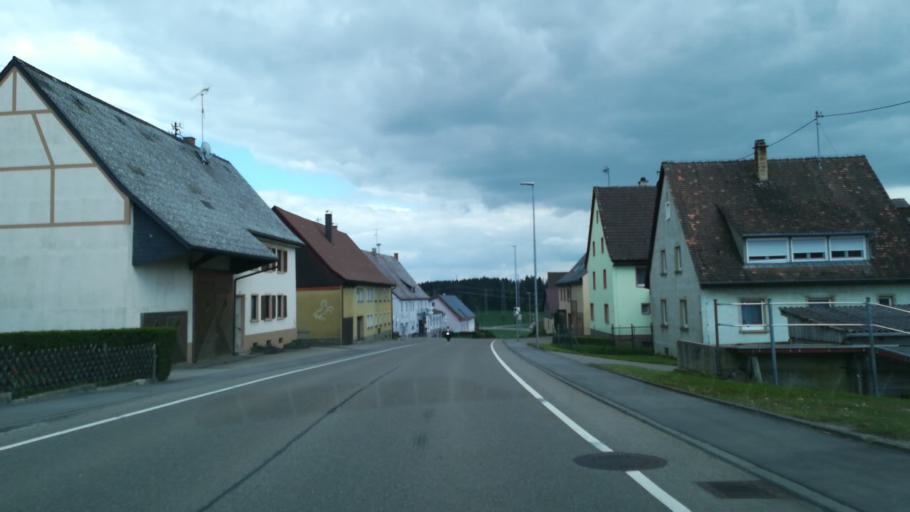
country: DE
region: Baden-Wuerttemberg
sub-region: Freiburg Region
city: Blumberg
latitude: 47.8206
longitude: 8.5754
